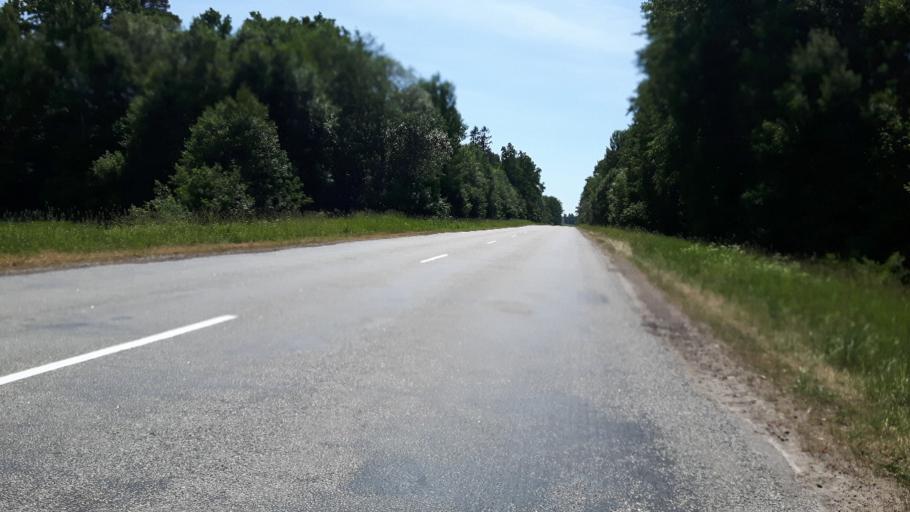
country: LV
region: Aizpute
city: Aizpute
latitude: 56.8170
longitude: 21.7247
